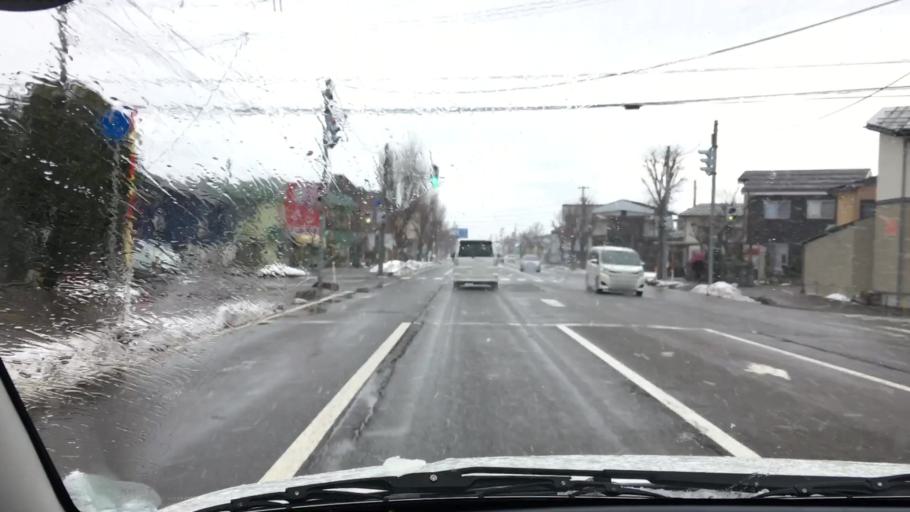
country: JP
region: Niigata
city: Joetsu
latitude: 37.1204
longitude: 138.2326
